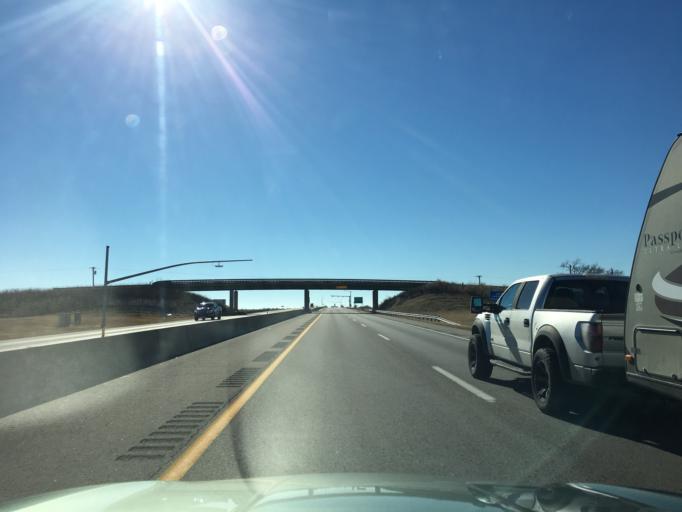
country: US
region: Oklahoma
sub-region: Kay County
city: Blackwell
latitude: 37.0002
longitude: -97.3424
